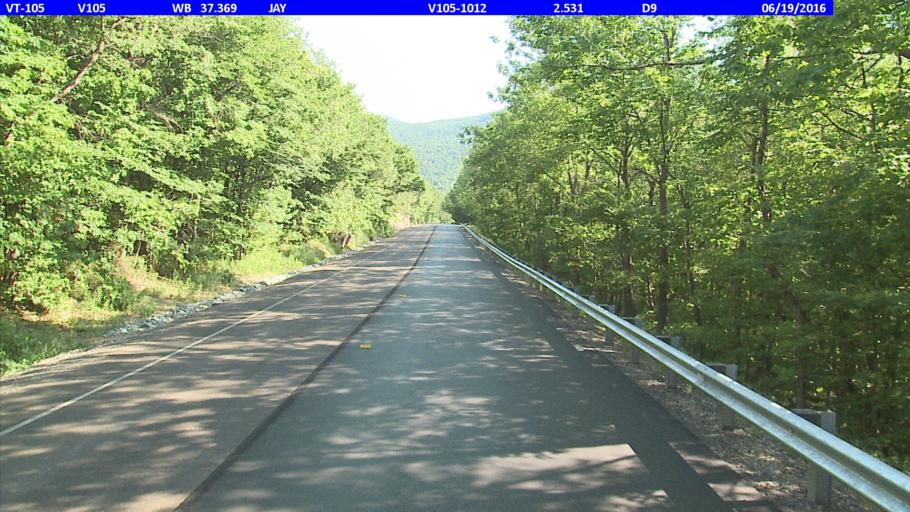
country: US
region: Vermont
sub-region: Franklin County
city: Richford
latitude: 44.9793
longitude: -72.5191
